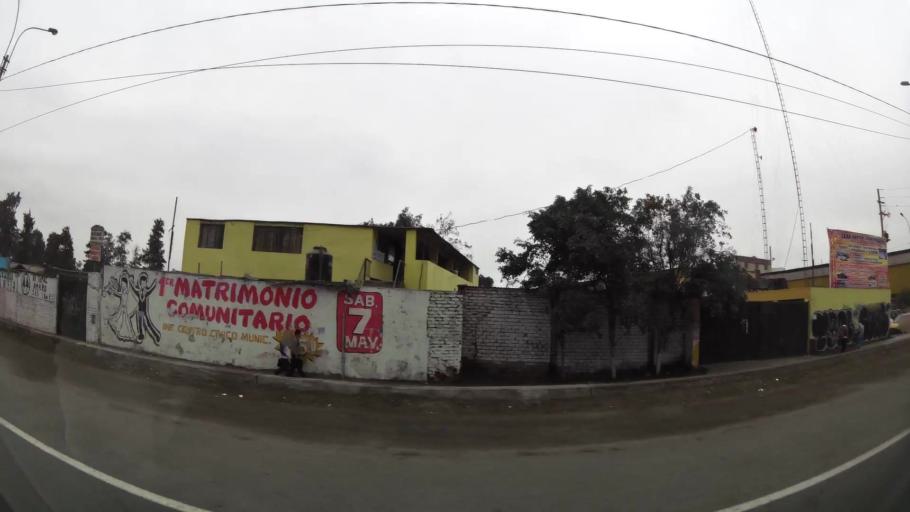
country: PE
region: Lima
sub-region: Lima
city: Independencia
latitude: -11.9628
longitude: -77.0549
